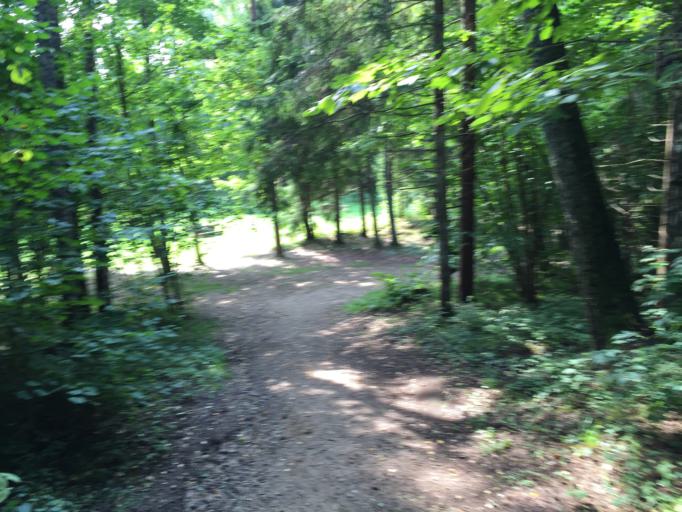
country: LV
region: Dagda
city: Dagda
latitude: 56.2696
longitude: 27.6573
